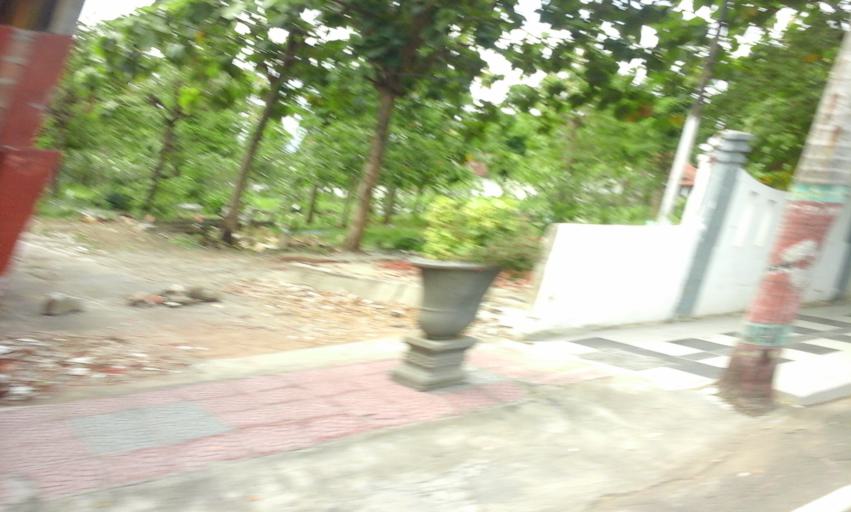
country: ID
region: East Java
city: Banyuwangi
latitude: -8.2246
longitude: 114.3668
